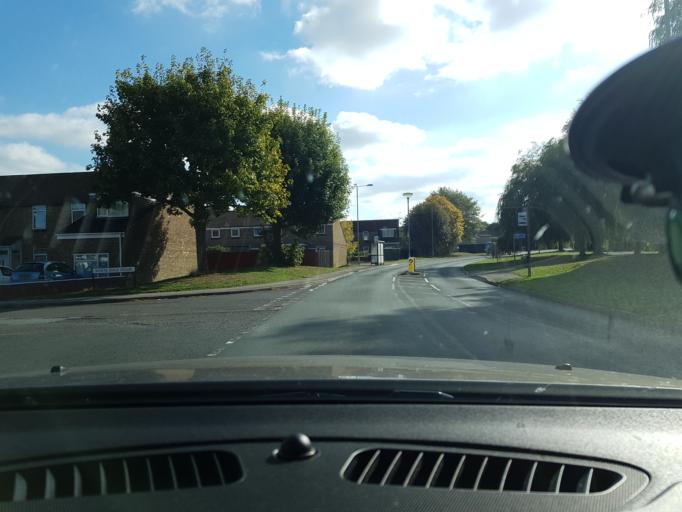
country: GB
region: England
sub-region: Borough of Swindon
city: Wanborough
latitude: 51.5464
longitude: -1.7269
